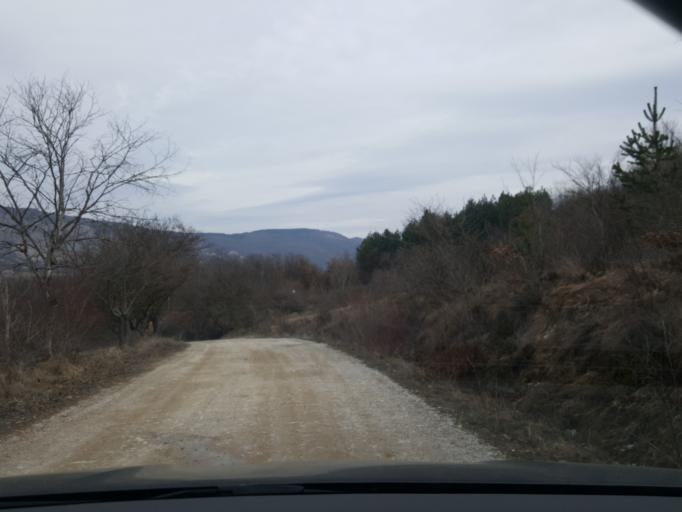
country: RS
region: Central Serbia
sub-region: Pirotski Okrug
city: Dimitrovgrad
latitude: 43.0038
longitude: 22.7515
